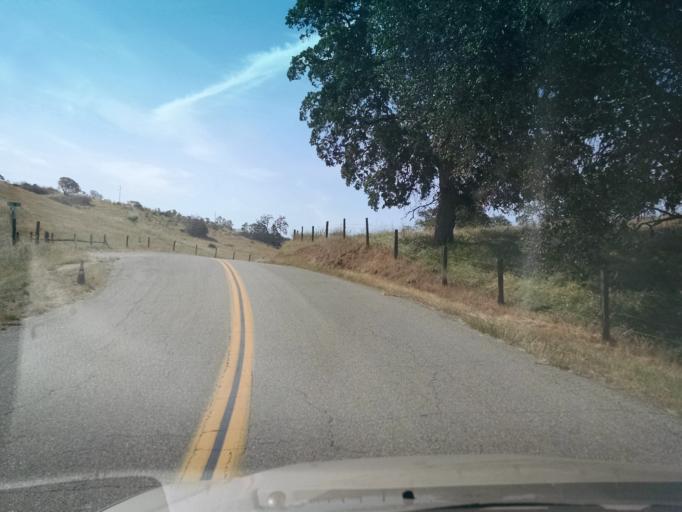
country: US
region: California
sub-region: Madera County
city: Yosemite Lakes
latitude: 37.1150
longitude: -119.6953
